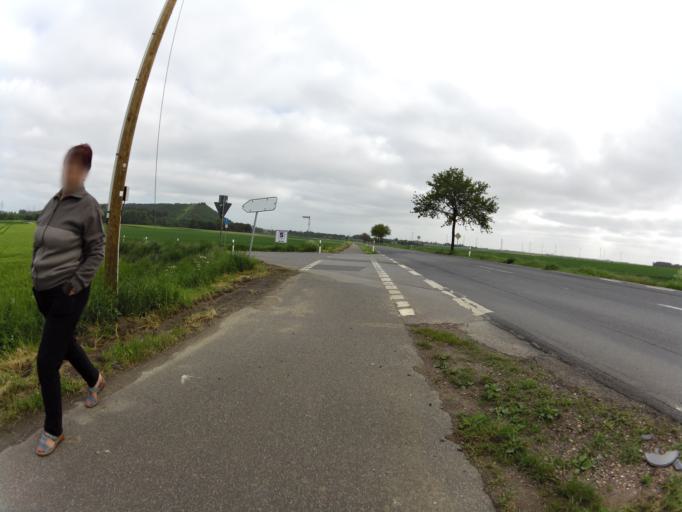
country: DE
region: North Rhine-Westphalia
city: Siersdorf
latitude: 50.9122
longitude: 6.2380
